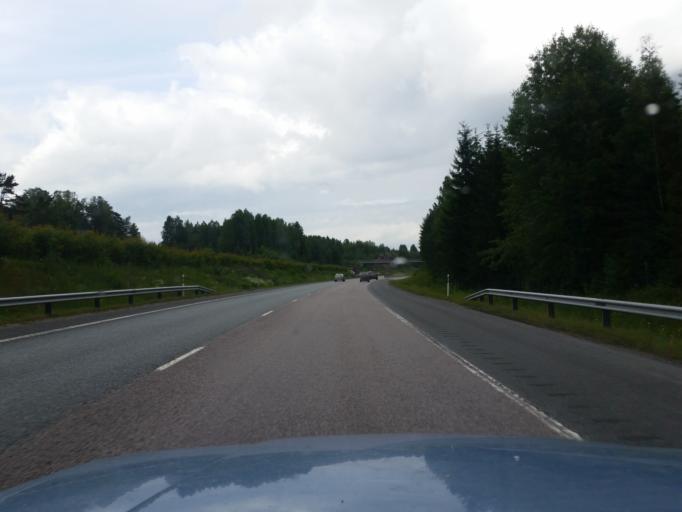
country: FI
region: Paijanne Tavastia
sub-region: Lahti
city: Nastola
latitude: 61.0907
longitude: 25.8964
